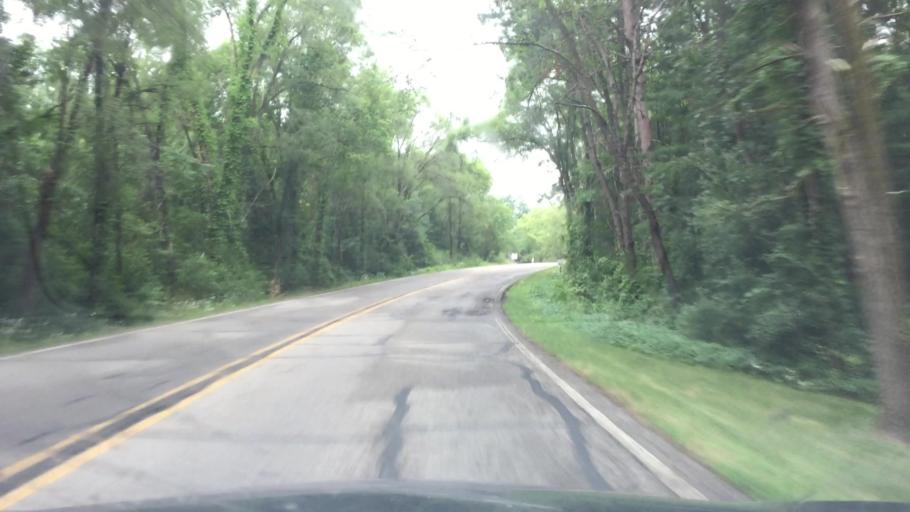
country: US
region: Michigan
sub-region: Oakland County
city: South Lyon
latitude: 42.5123
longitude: -83.6871
